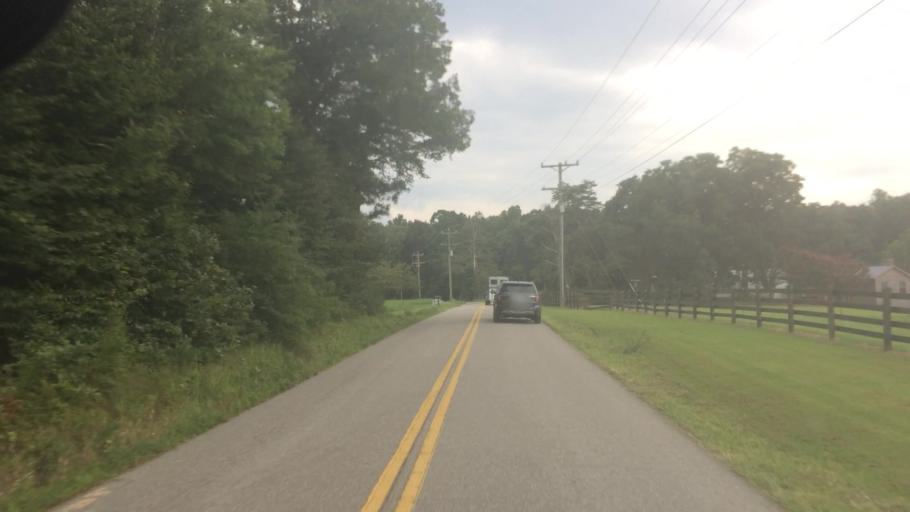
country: US
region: Virginia
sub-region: King William County
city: West Point
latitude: 37.5689
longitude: -76.7064
